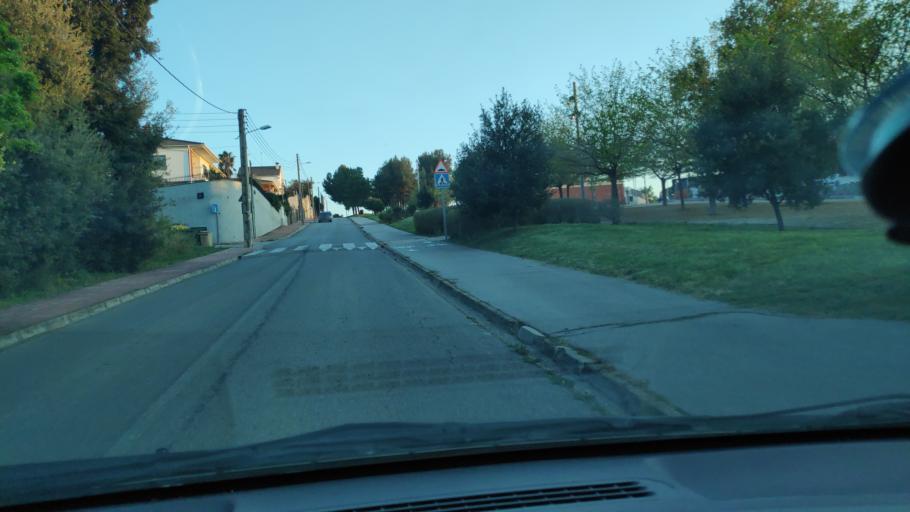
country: ES
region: Catalonia
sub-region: Provincia de Barcelona
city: Sant Quirze del Valles
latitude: 41.5342
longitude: 2.0483
